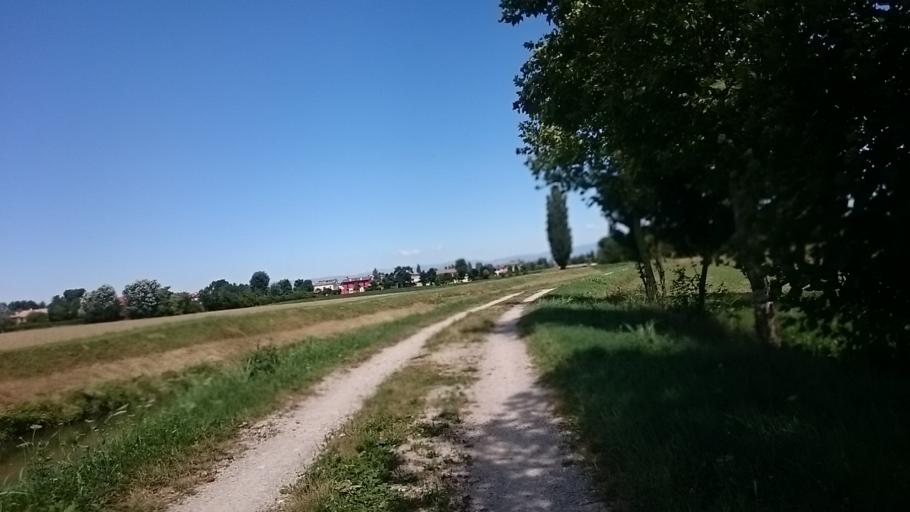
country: IT
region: Veneto
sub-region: Provincia di Padova
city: Codiverno
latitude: 45.4747
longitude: 11.9505
